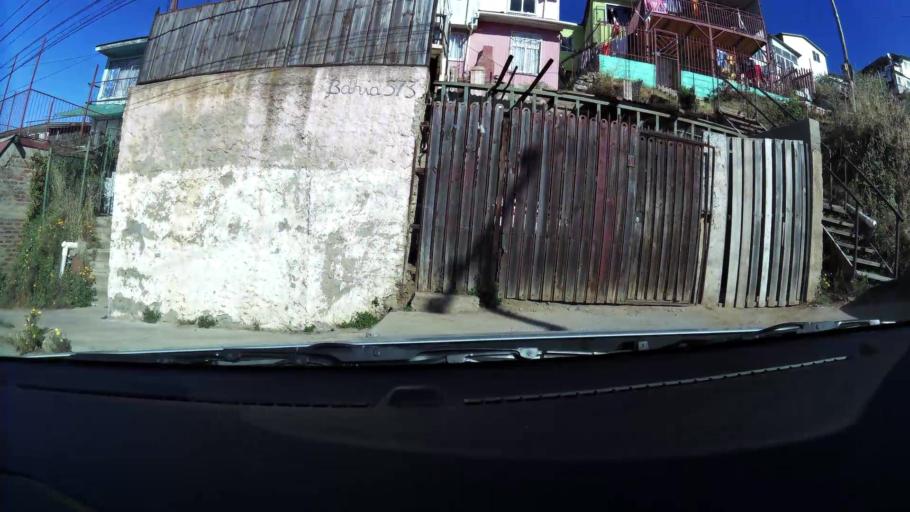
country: CL
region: Valparaiso
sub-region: Provincia de Valparaiso
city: Valparaiso
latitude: -33.0581
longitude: -71.6225
